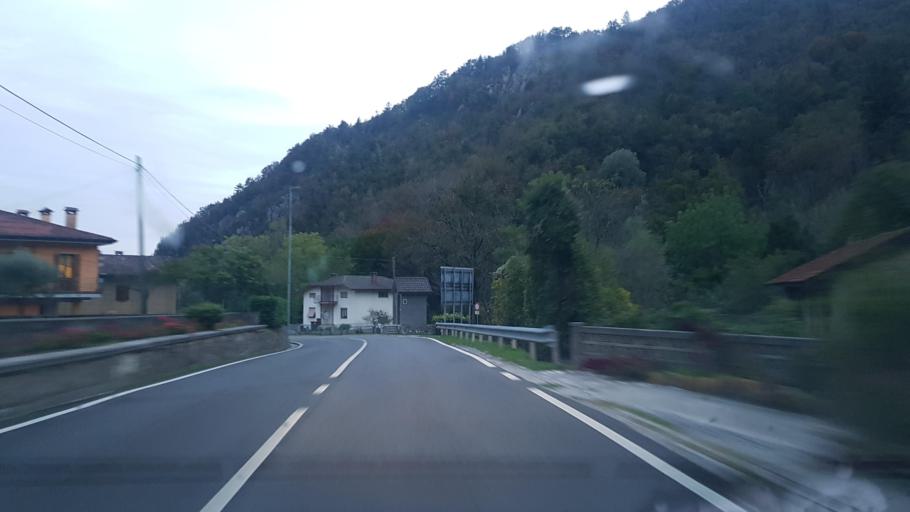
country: IT
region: Friuli Venezia Giulia
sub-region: Provincia di Pordenone
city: Anduins
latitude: 46.2162
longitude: 12.9543
